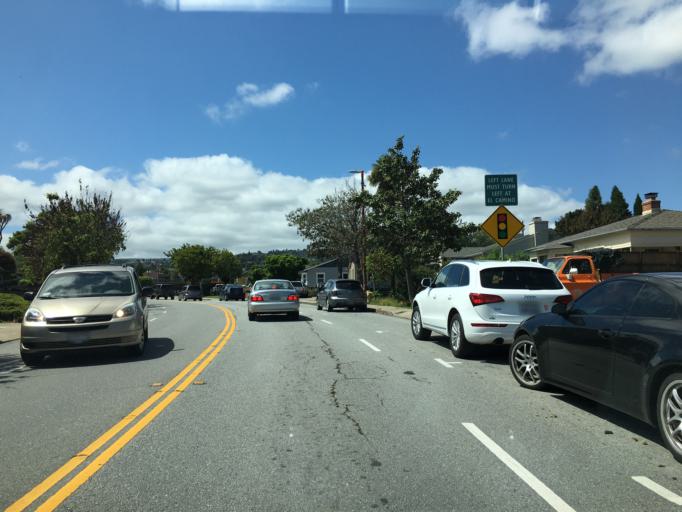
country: US
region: California
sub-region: San Mateo County
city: San Carlos
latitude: 37.5104
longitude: -122.2600
